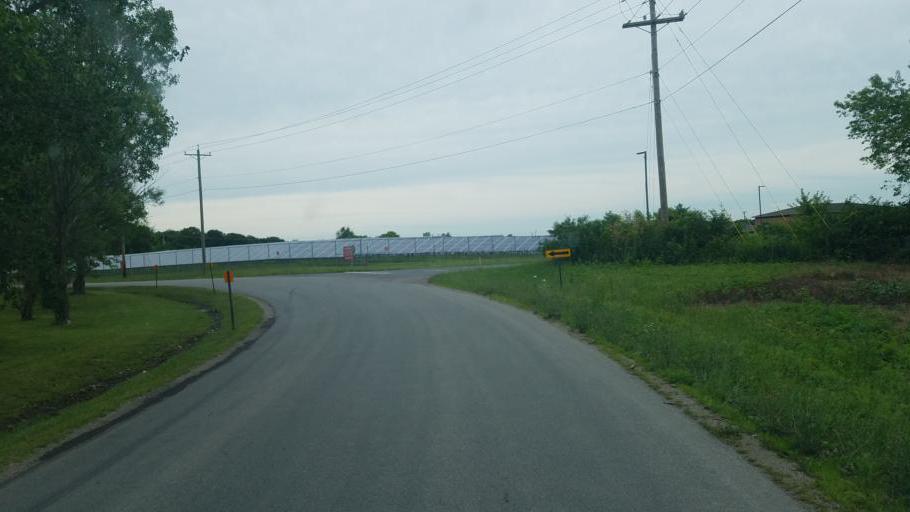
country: US
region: Ohio
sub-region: Knox County
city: Centerburg
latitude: 40.2923
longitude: -82.7063
